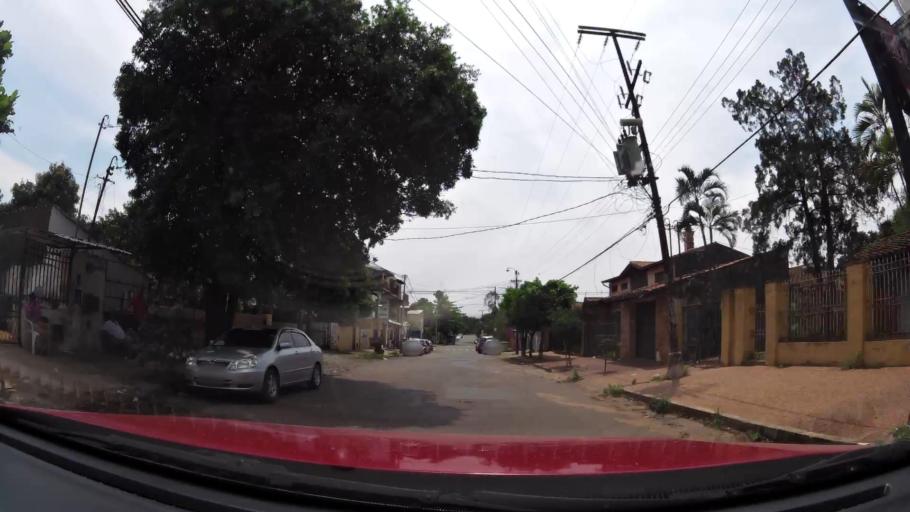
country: PY
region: Central
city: Fernando de la Mora
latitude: -25.3160
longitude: -57.5607
